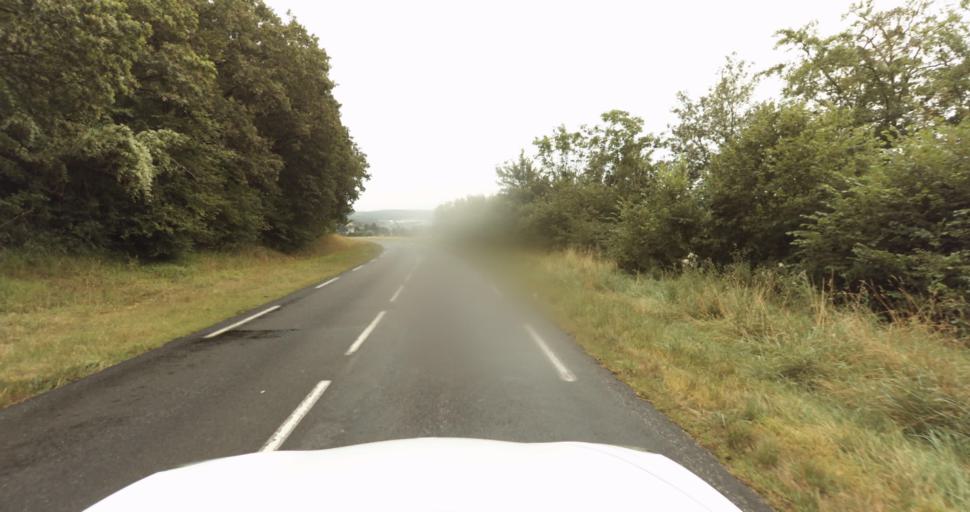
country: FR
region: Haute-Normandie
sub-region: Departement de l'Eure
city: Normanville
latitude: 49.0775
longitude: 1.1707
